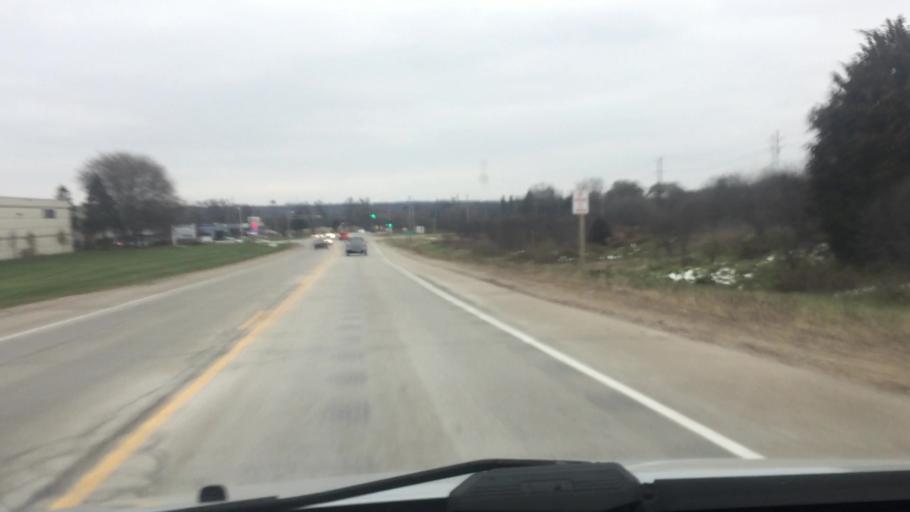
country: US
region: Wisconsin
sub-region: Waukesha County
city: Hartland
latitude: 43.0959
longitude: -88.3620
